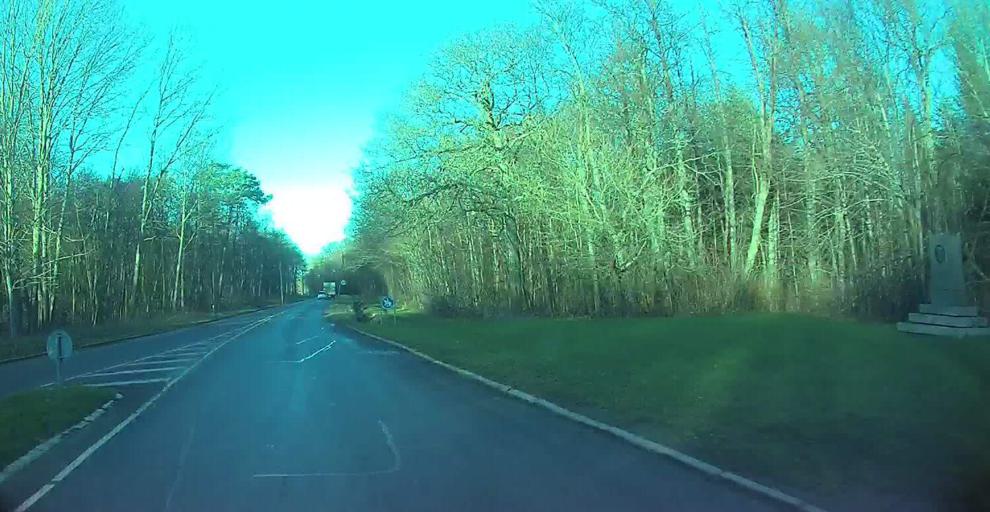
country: DK
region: Capital Region
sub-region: Tarnby Kommune
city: Tarnby
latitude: 55.5748
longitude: 12.5796
